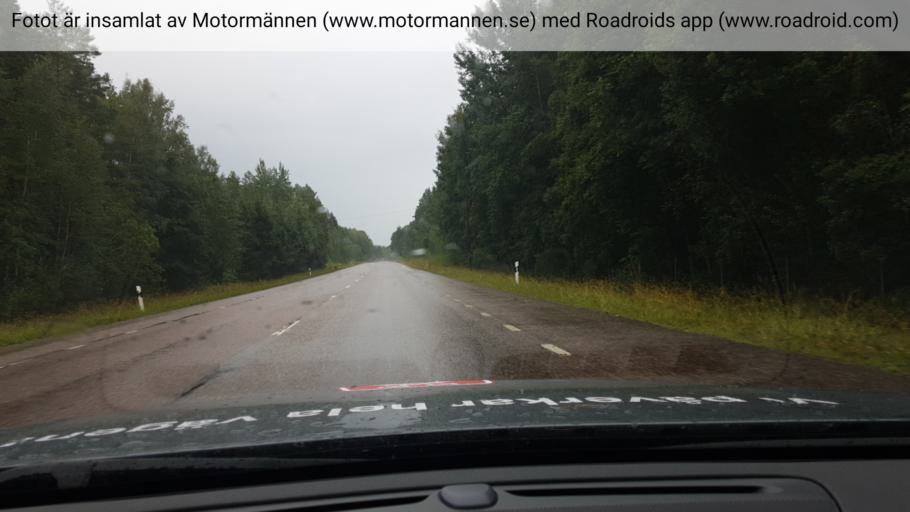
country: SE
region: Uppsala
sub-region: Alvkarleby Kommun
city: AElvkarleby
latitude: 60.5927
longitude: 17.4629
